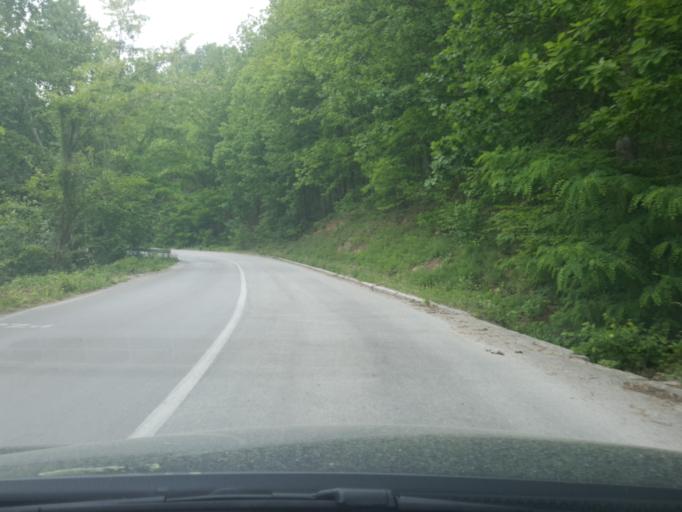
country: RS
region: Central Serbia
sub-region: Zlatiborski Okrug
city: Bajina Basta
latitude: 43.9437
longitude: 19.5605
